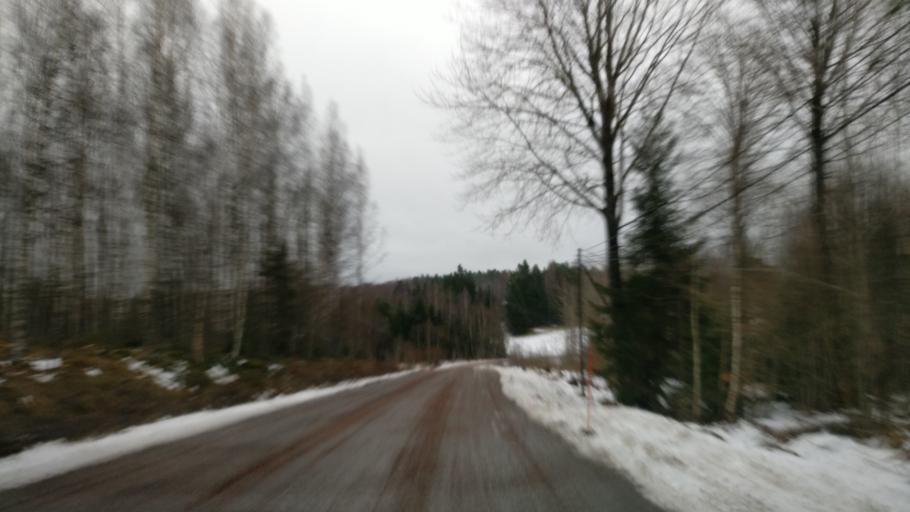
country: FI
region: Uusimaa
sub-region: Raaseporin
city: Karis
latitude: 60.0788
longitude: 23.7975
